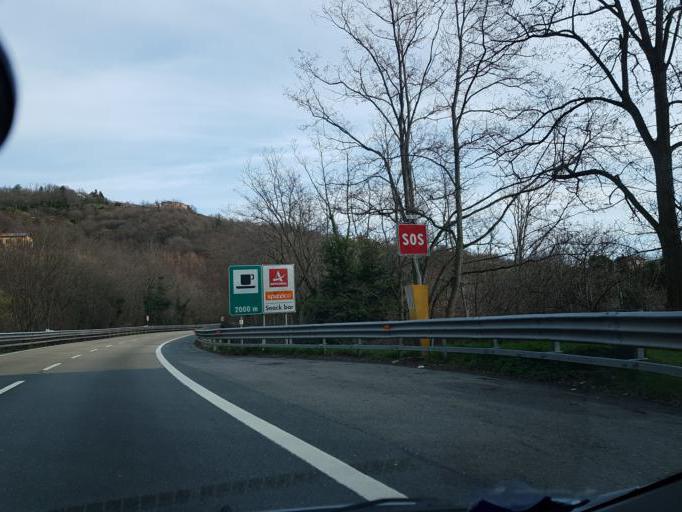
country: IT
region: Liguria
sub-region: Provincia di Genova
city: Pedemonte
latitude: 44.5115
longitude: 8.9264
